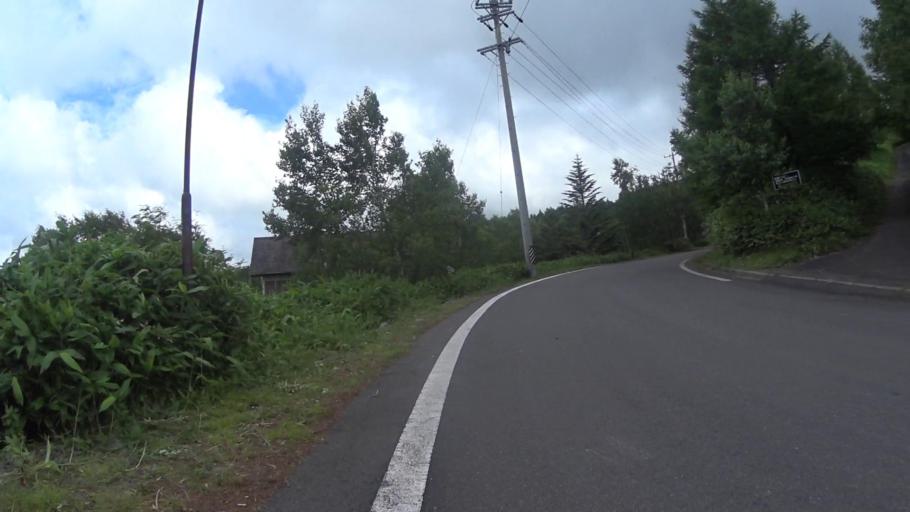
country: JP
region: Nagano
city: Saku
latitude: 36.1183
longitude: 138.3350
